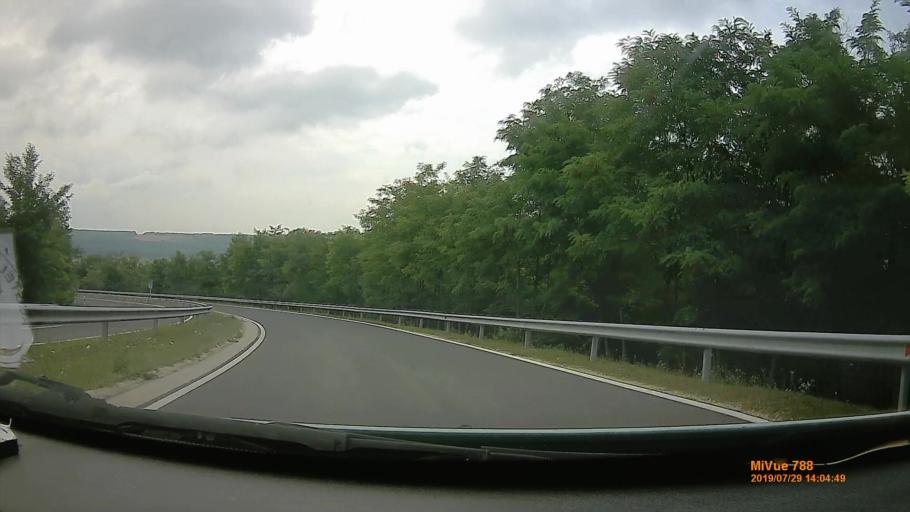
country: HU
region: Somogy
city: Balatonfoldvar
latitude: 46.8154
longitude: 17.9156
